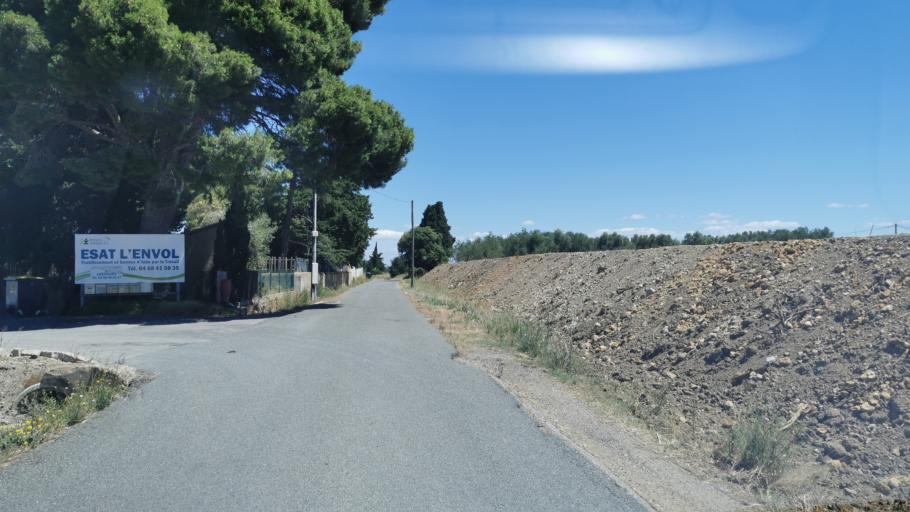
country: FR
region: Languedoc-Roussillon
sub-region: Departement de l'Aude
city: Narbonne
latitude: 43.1600
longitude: 2.9954
